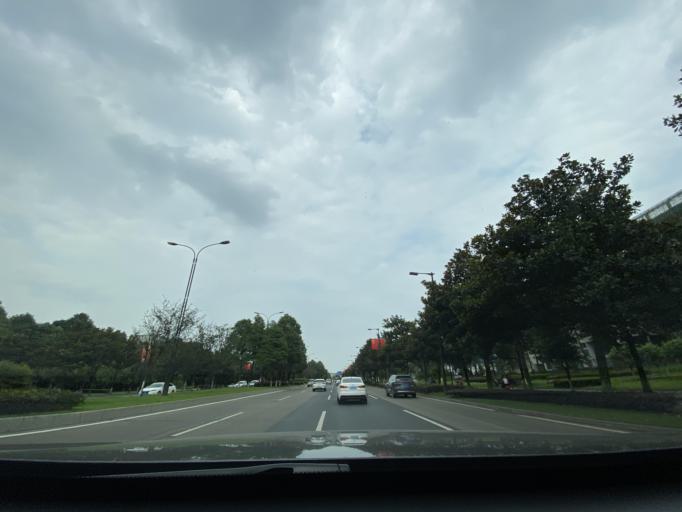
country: CN
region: Sichuan
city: Dongsheng
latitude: 30.6054
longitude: 103.9308
